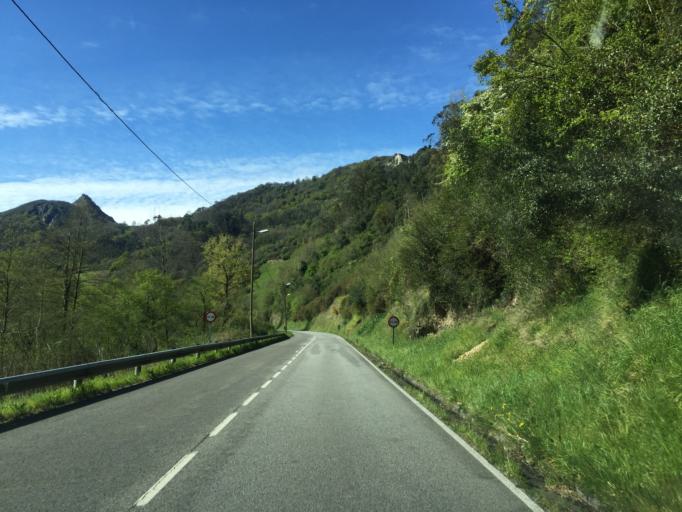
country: ES
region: Asturias
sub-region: Province of Asturias
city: Proaza
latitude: 43.3270
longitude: -5.9902
